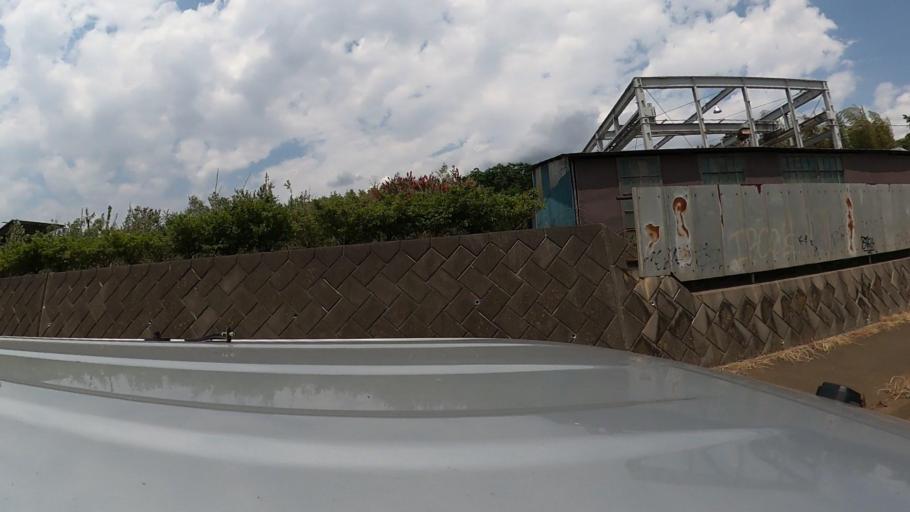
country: JP
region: Kanagawa
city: Chigasaki
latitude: 35.3853
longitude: 139.4194
